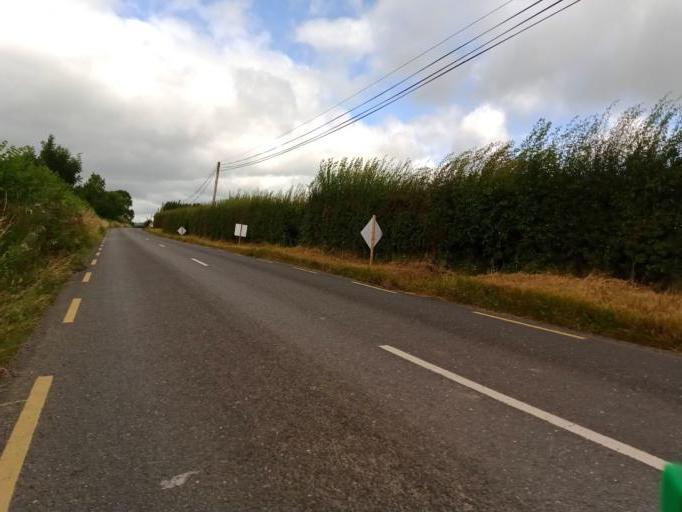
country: IE
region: Leinster
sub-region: Kilkenny
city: Callan
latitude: 52.5558
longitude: -7.4094
